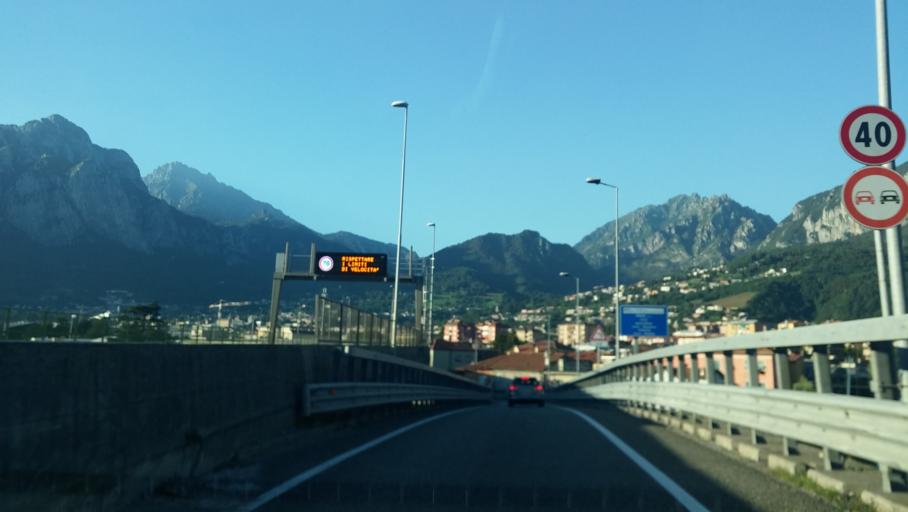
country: IT
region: Lombardy
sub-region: Provincia di Lecco
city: Pescate
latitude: 45.8432
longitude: 9.4055
